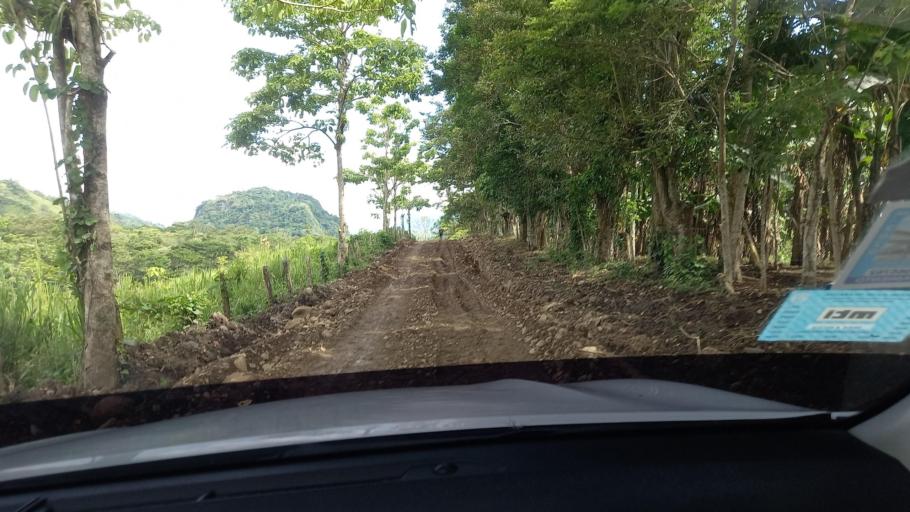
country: NI
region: Jinotega
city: San Jose de Bocay
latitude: 13.3861
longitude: -85.6892
